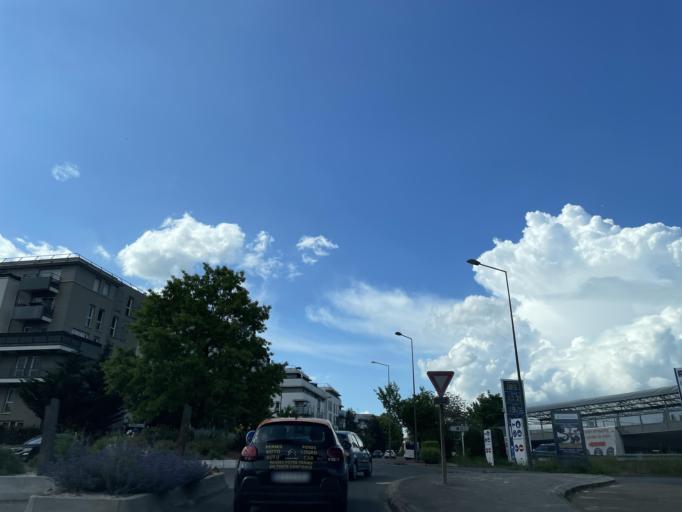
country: FR
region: Ile-de-France
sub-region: Departement du Val-d'Oise
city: Arnouville
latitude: 48.9746
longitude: 2.4167
